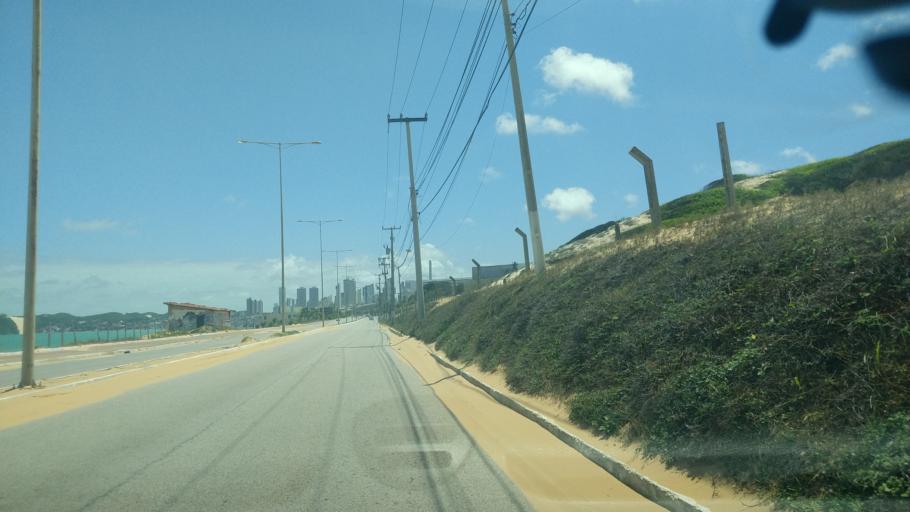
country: BR
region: Rio Grande do Norte
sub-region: Natal
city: Natal
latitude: -5.8564
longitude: -35.1819
